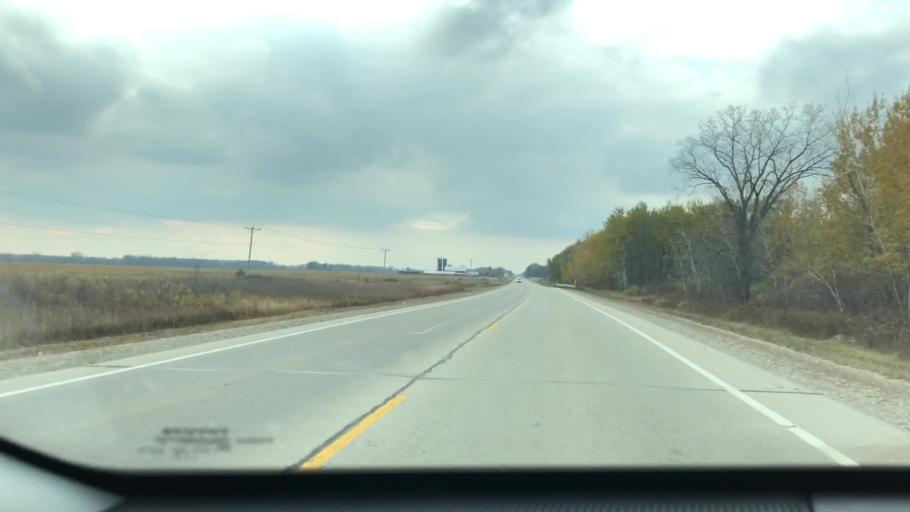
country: US
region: Wisconsin
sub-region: Brown County
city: Oneida
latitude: 44.5024
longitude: -88.2414
